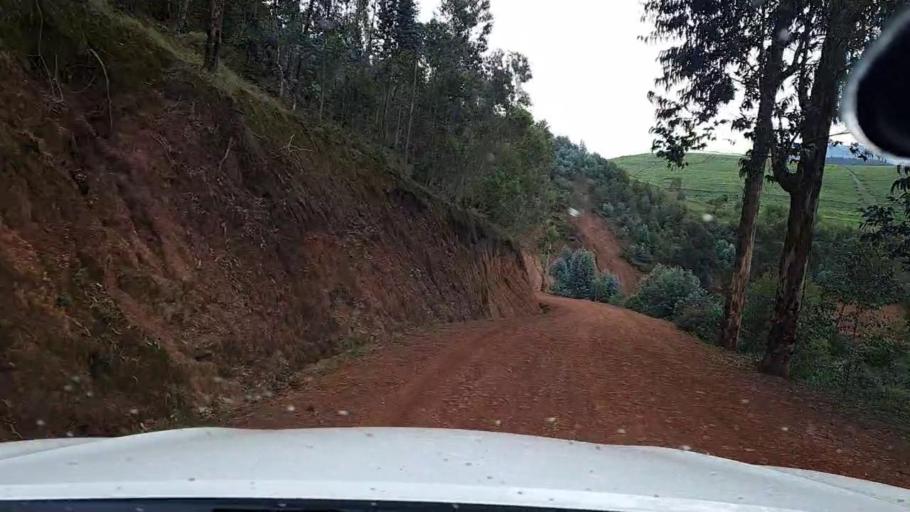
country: RW
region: Western Province
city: Kibuye
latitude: -2.1699
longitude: 29.4352
